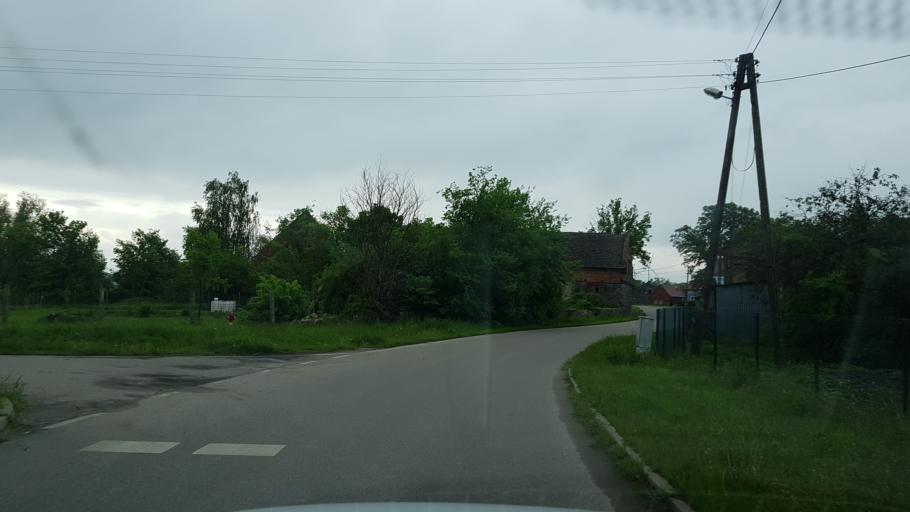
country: PL
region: West Pomeranian Voivodeship
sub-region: Powiat pyrzycki
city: Bielice
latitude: 53.1336
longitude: 14.7476
